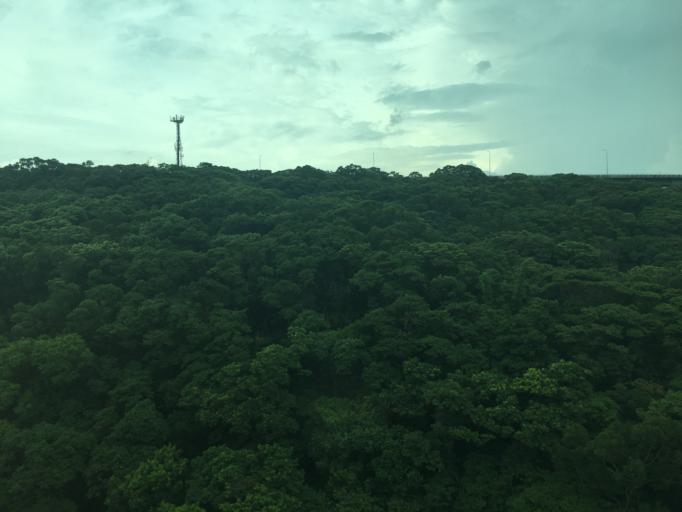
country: TW
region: Taiwan
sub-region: Taoyuan
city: Taoyuan
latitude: 25.0681
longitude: 121.3447
